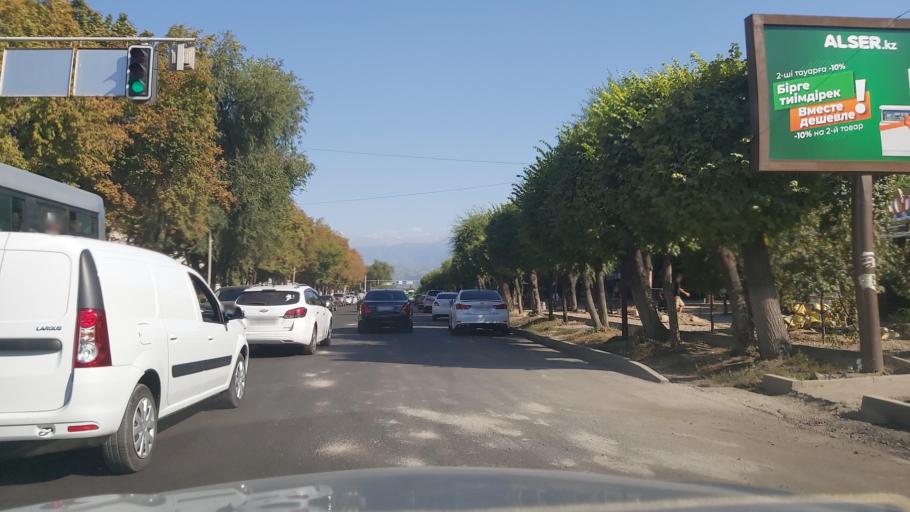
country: KZ
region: Almaty Oblysy
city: Pervomayskiy
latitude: 43.3228
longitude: 76.9121
